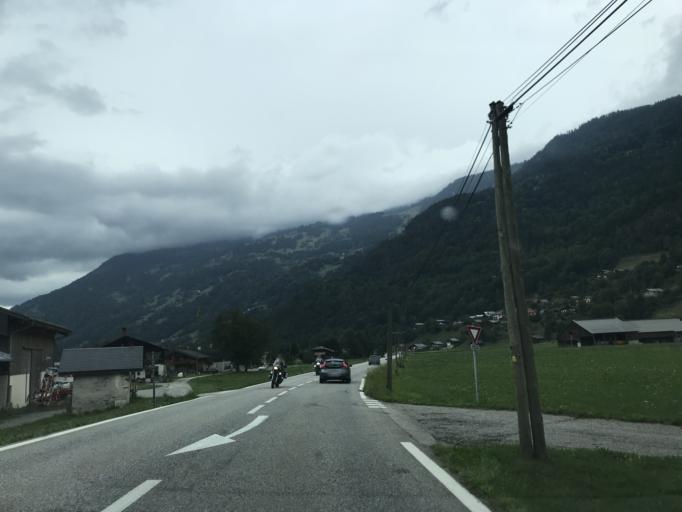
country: FR
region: Rhone-Alpes
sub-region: Departement de la Savoie
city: Beaufort
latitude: 45.7214
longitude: 6.5581
